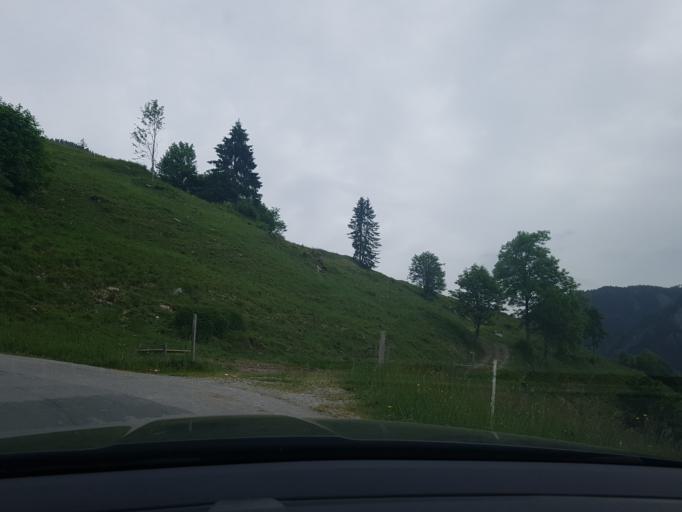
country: AT
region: Salzburg
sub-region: Politischer Bezirk Sankt Johann im Pongau
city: Schwarzach im Pongau
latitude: 47.2780
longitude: 13.2069
